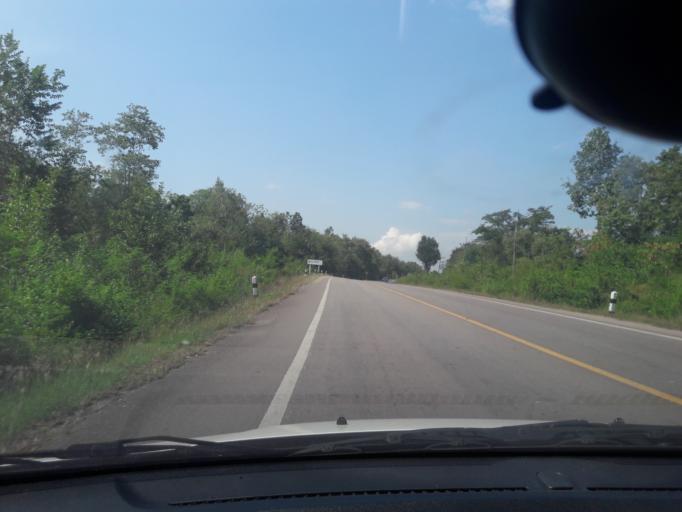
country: TH
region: Lampang
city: Mae Tha
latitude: 18.1886
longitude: 99.5347
